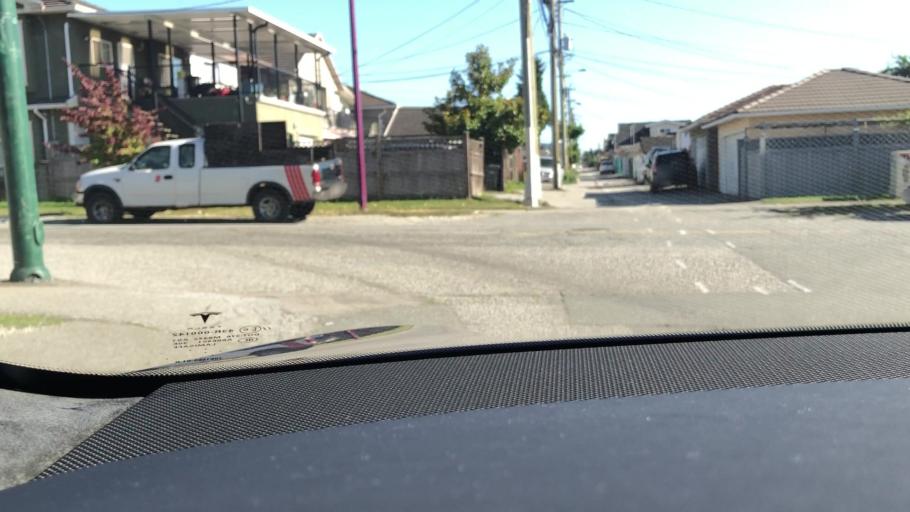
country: CA
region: British Columbia
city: Vancouver
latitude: 49.2307
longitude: -123.0663
